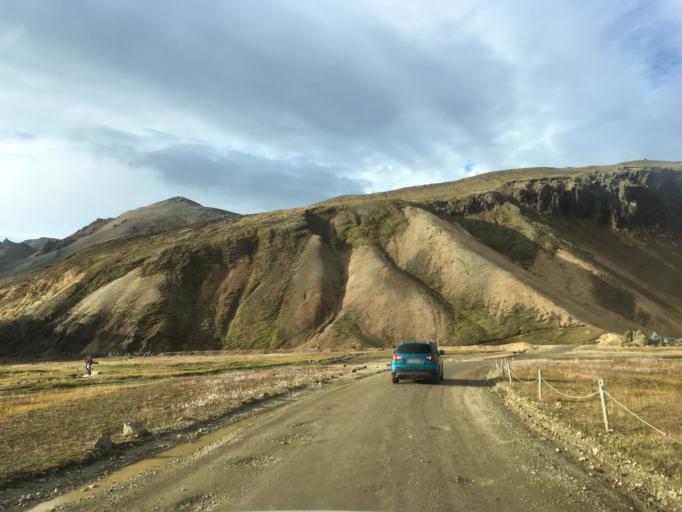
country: IS
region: South
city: Vestmannaeyjar
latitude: 63.9931
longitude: -19.0596
